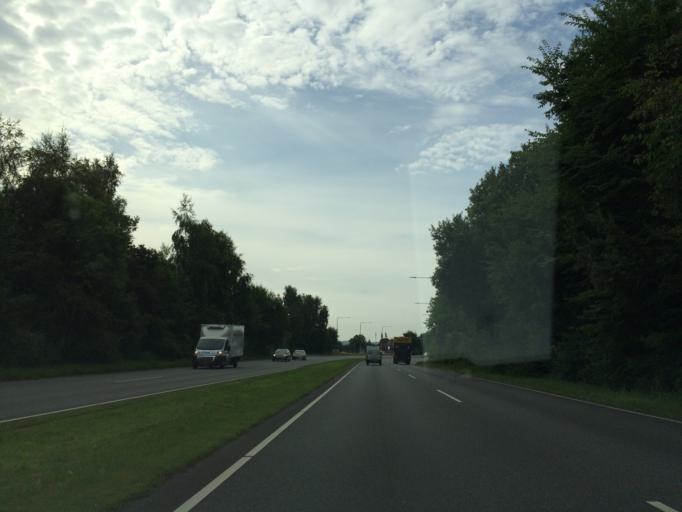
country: DK
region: South Denmark
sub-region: Kolding Kommune
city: Kolding
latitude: 55.5097
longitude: 9.5037
